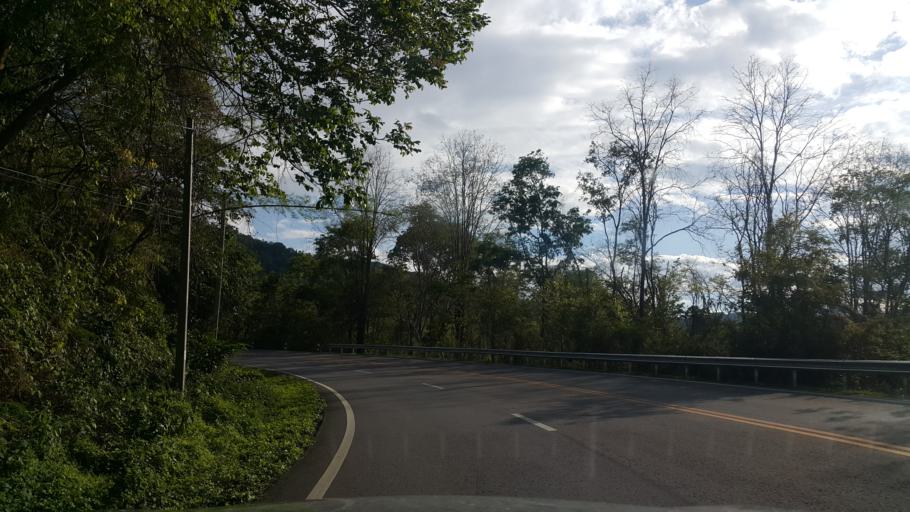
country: TH
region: Phayao
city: Phayao
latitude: 19.0701
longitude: 99.8112
